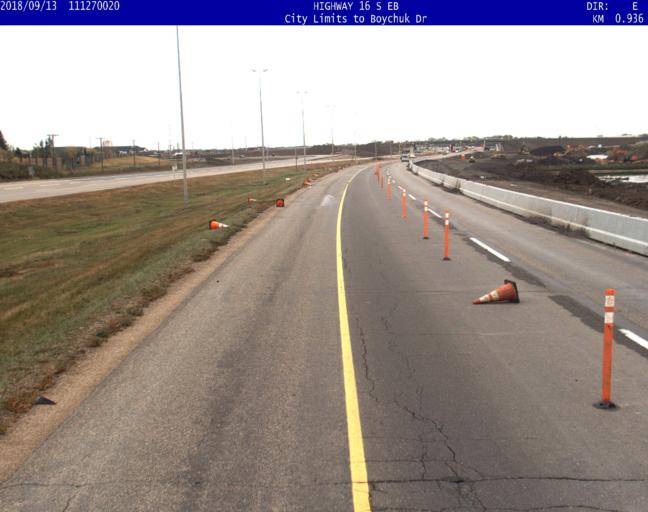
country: CA
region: Saskatchewan
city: Saskatoon
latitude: 52.0890
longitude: -106.5841
